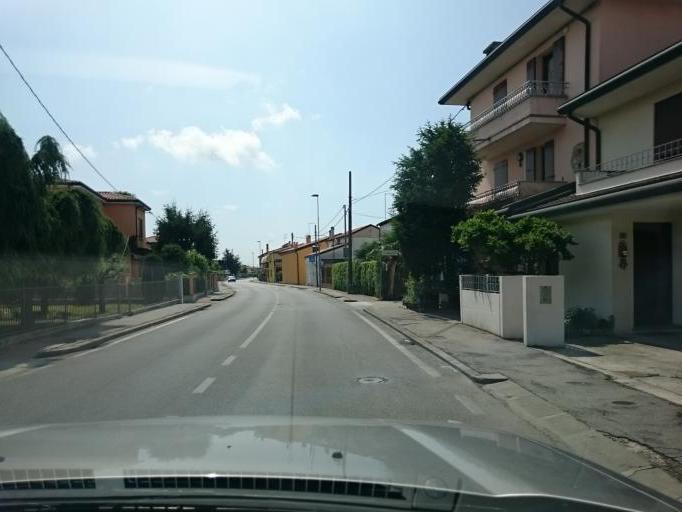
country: IT
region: Veneto
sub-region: Provincia di Padova
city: Albignasego
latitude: 45.3448
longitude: 11.8700
